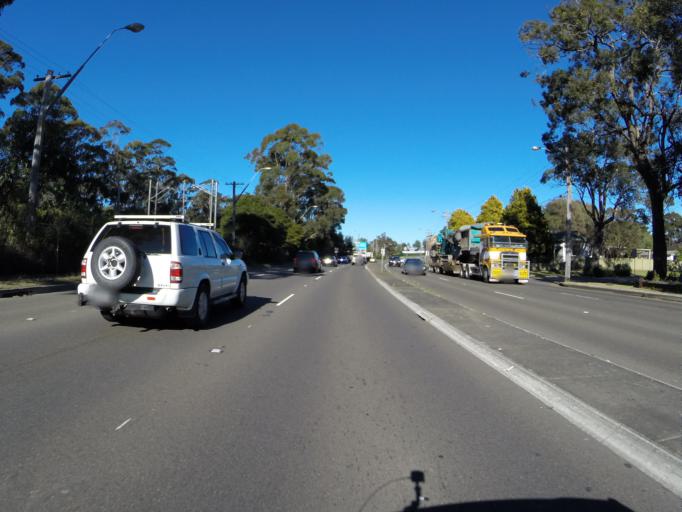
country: AU
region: New South Wales
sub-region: Sutherland Shire
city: Heathcote
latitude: -34.0839
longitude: 151.0111
